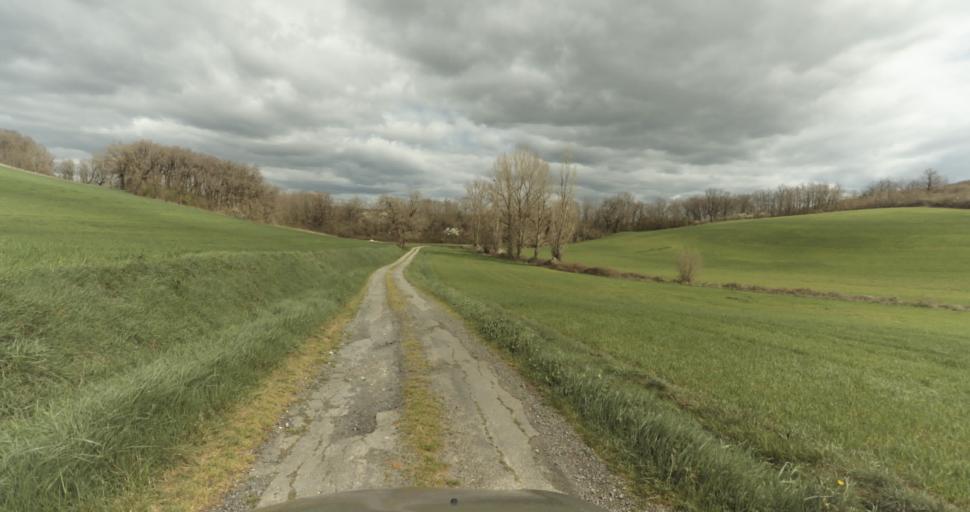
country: FR
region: Midi-Pyrenees
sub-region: Departement du Tarn
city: Puygouzon
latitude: 43.8778
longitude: 2.1627
